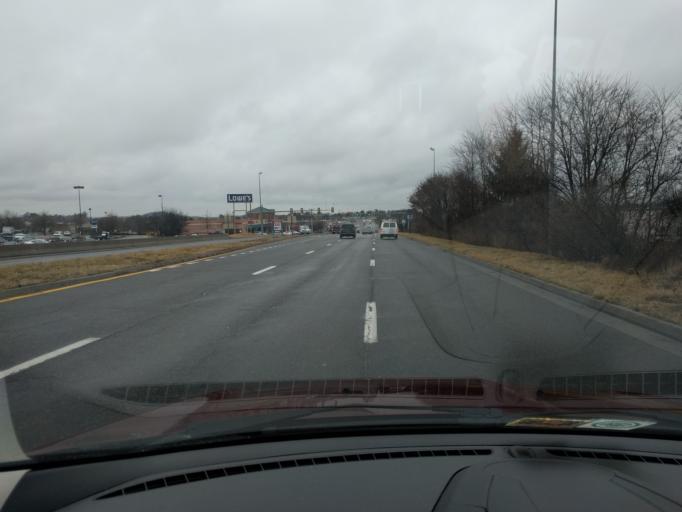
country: US
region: Virginia
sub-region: Montgomery County
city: Merrimac
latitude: 37.1647
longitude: -80.4165
